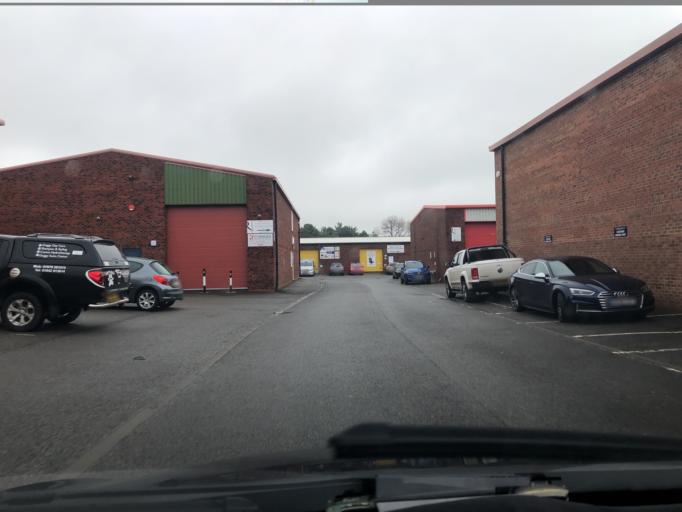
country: GB
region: England
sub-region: North Yorkshire
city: Stokesley
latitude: 54.4620
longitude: -1.1792
